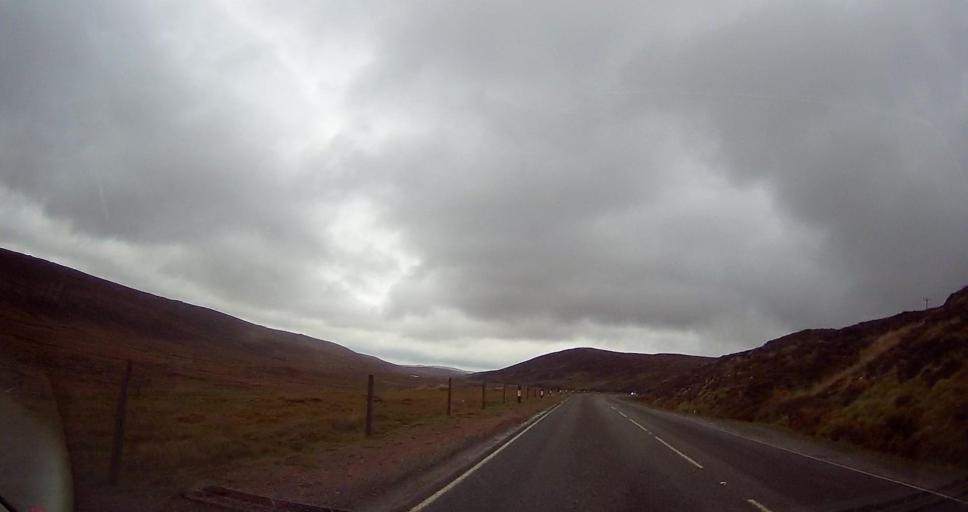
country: GB
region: Scotland
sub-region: Shetland Islands
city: Lerwick
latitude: 60.2953
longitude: -1.2395
